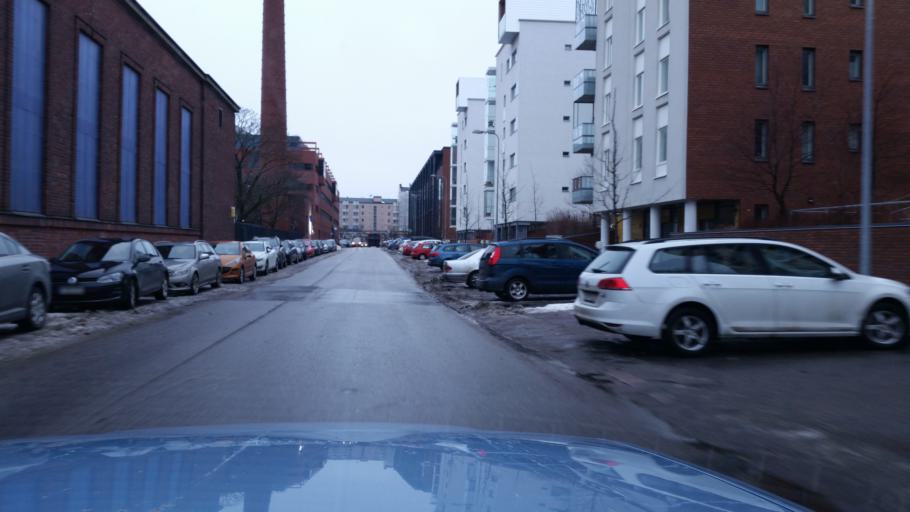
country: FI
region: Uusimaa
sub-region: Helsinki
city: Helsinki
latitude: 60.1911
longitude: 24.9704
